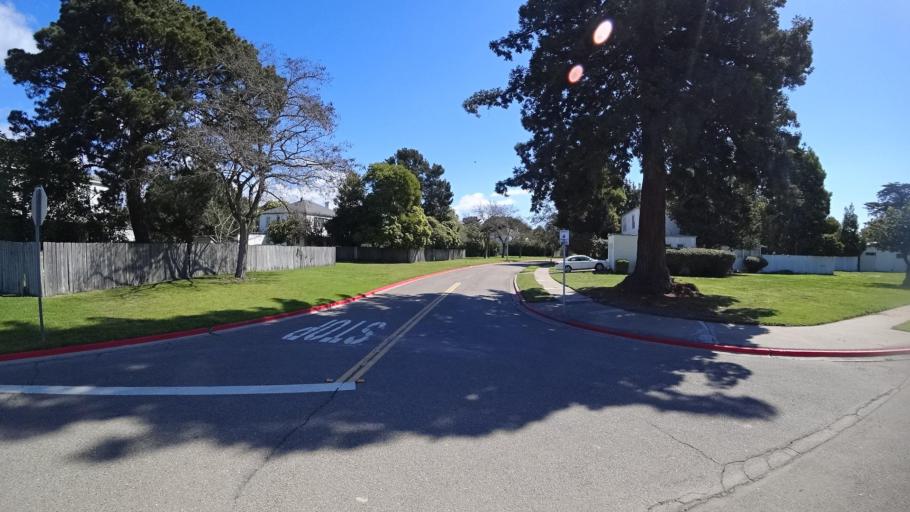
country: US
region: California
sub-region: Alameda County
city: Oakland
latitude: 37.7879
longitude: -122.2979
